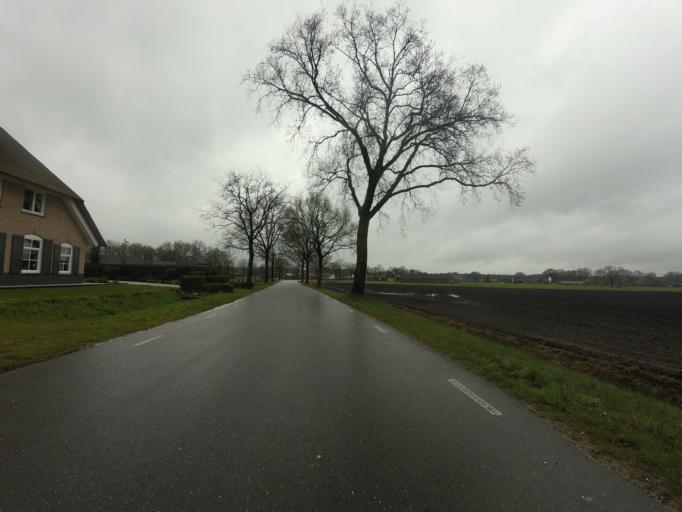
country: NL
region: Gelderland
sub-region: Gemeente Apeldoorn
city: Uddel
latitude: 52.2935
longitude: 5.7753
